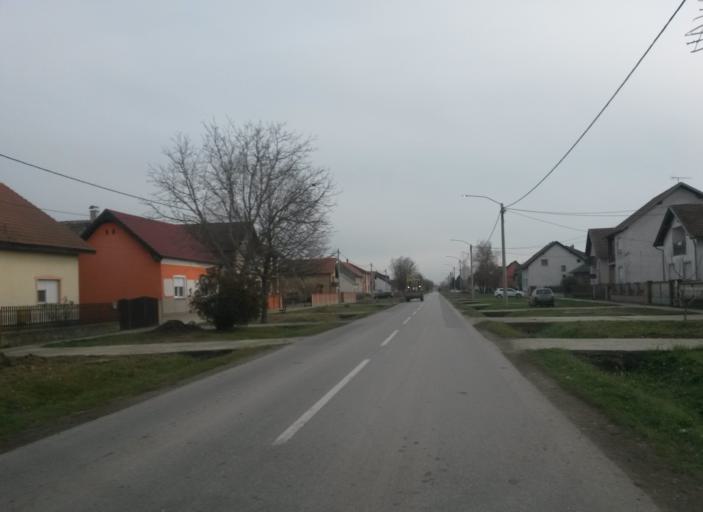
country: HR
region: Osjecko-Baranjska
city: Antunovac
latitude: 45.4828
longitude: 18.6419
